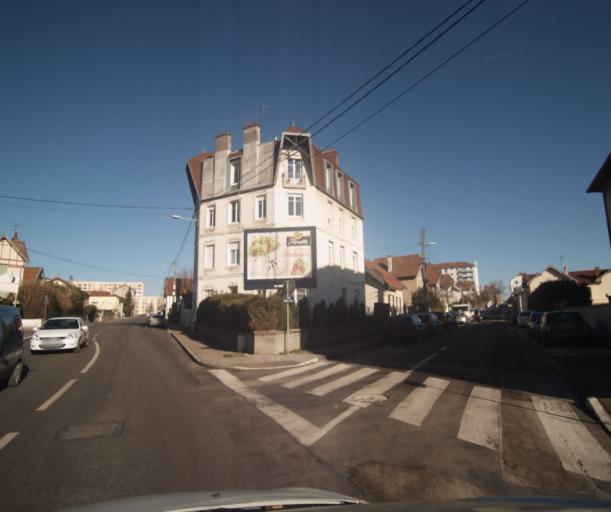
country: FR
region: Franche-Comte
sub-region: Departement du Doubs
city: Besancon
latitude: 47.2377
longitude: 6.0065
